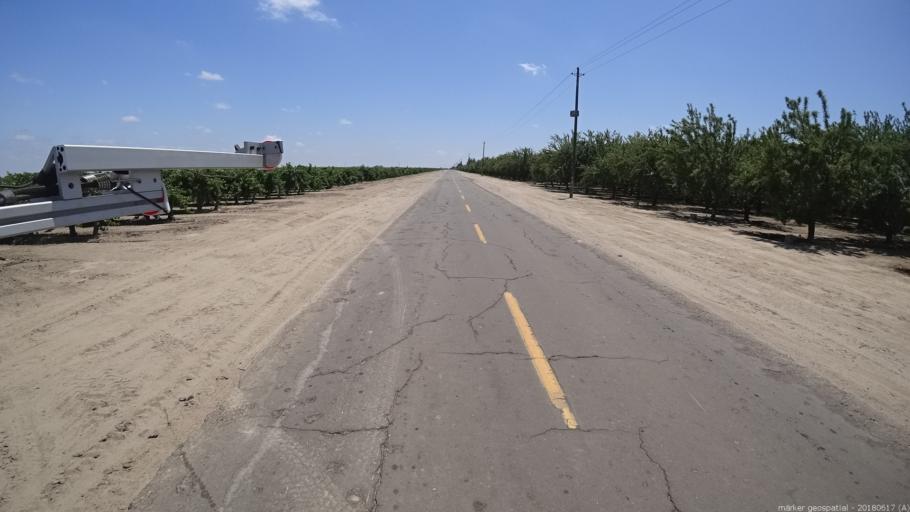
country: US
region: California
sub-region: Fresno County
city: Biola
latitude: 36.8275
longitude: -120.1509
